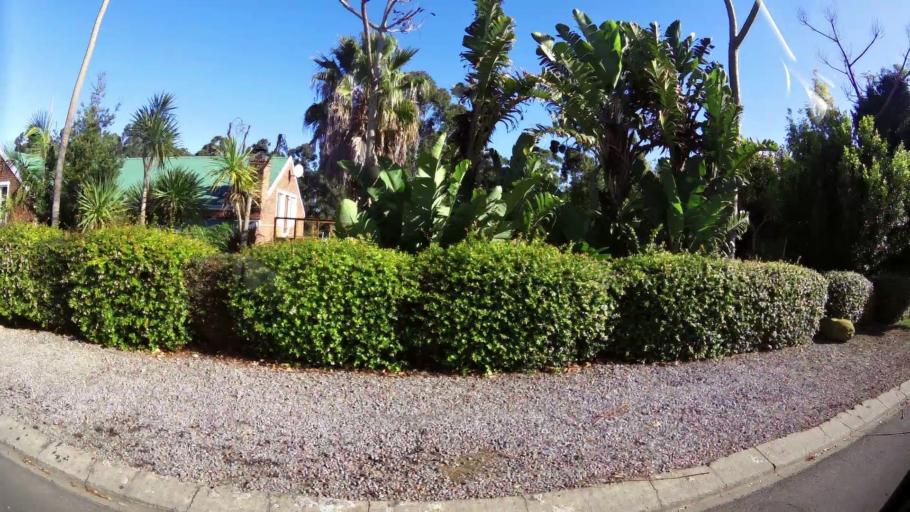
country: ZA
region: Western Cape
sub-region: Eden District Municipality
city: George
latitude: -33.9574
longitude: 22.4203
